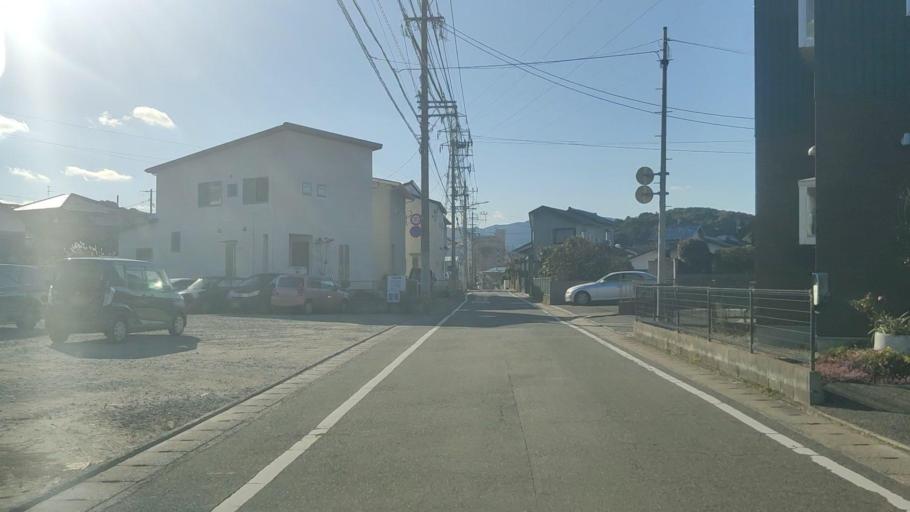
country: JP
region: Fukuoka
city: Fukuoka-shi
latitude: 33.5413
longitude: 130.3525
